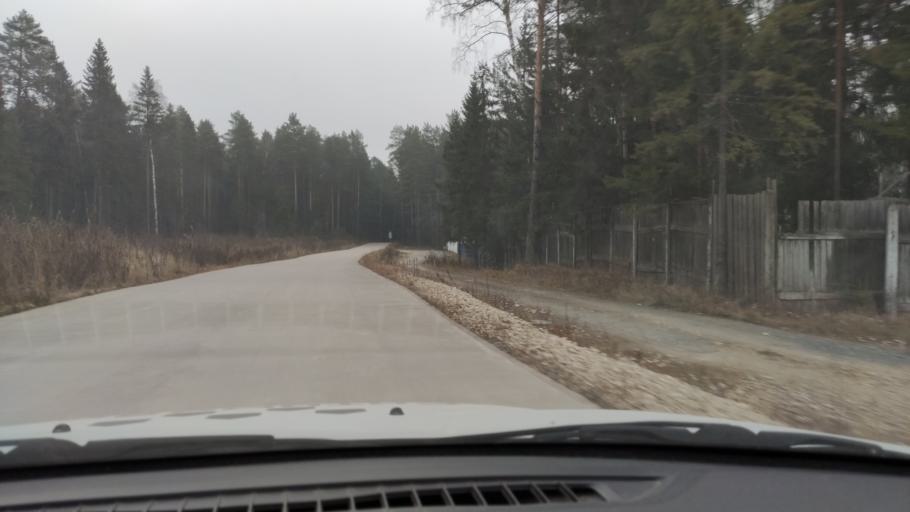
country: RU
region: Perm
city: Kondratovo
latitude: 58.0472
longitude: 56.1414
